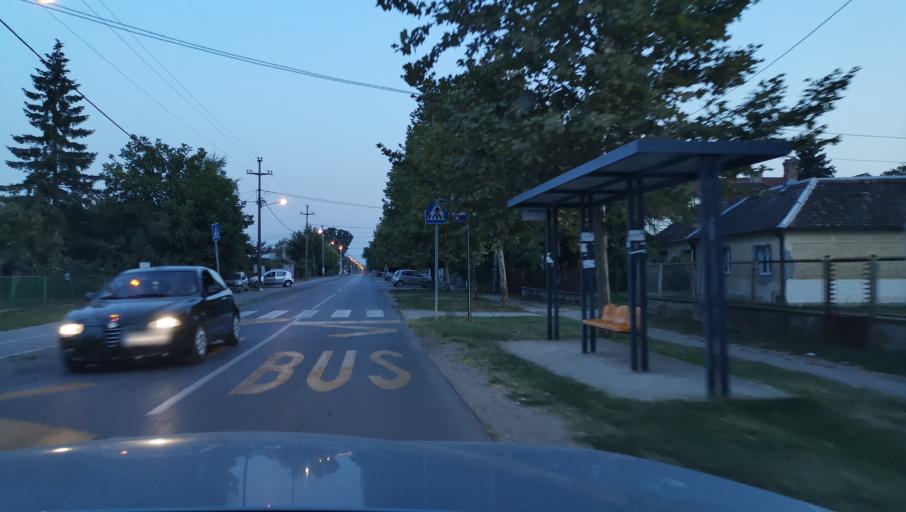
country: RS
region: Central Serbia
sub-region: Belgrade
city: Obrenovac
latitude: 44.6754
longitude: 20.2027
